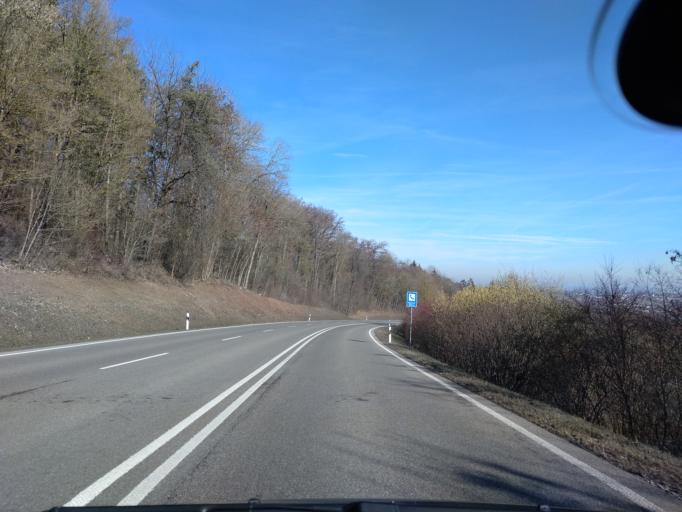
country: DE
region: Baden-Wuerttemberg
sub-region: Regierungsbezirk Stuttgart
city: Michelfeld
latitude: 49.0948
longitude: 9.6516
